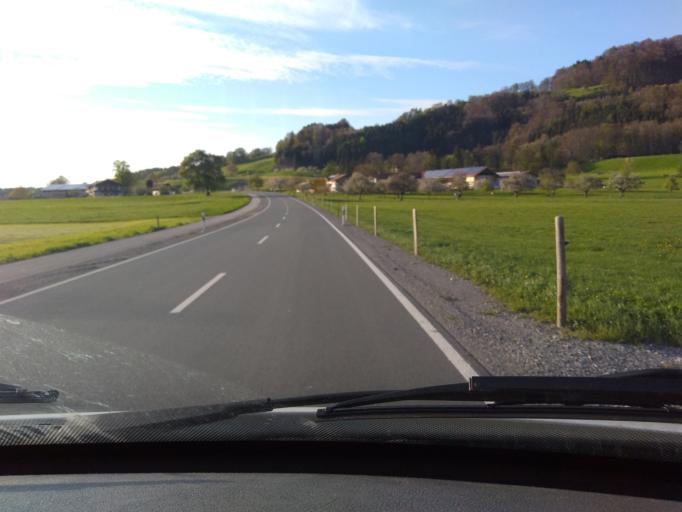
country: DE
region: Bavaria
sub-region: Upper Bavaria
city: Nussdorf am Inn
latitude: 47.7509
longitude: 12.1504
